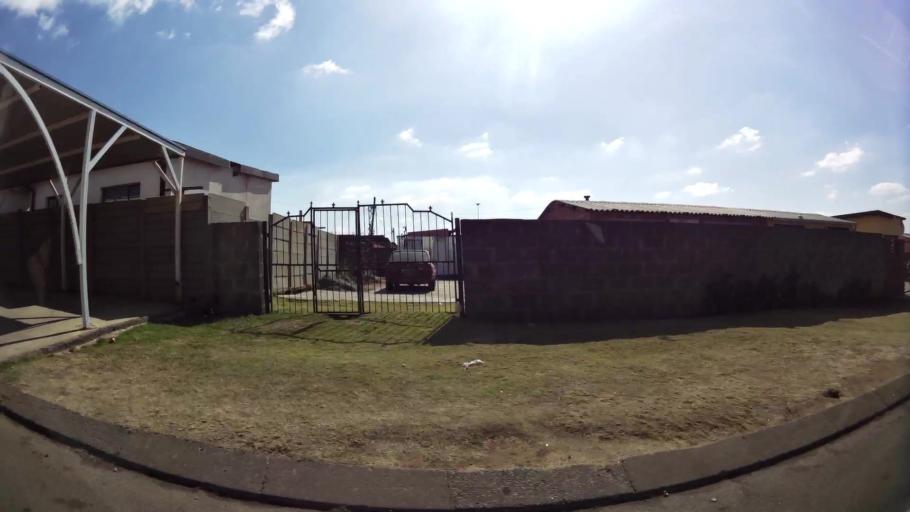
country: ZA
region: Gauteng
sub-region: City of Johannesburg Metropolitan Municipality
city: Soweto
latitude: -26.2501
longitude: 27.8854
